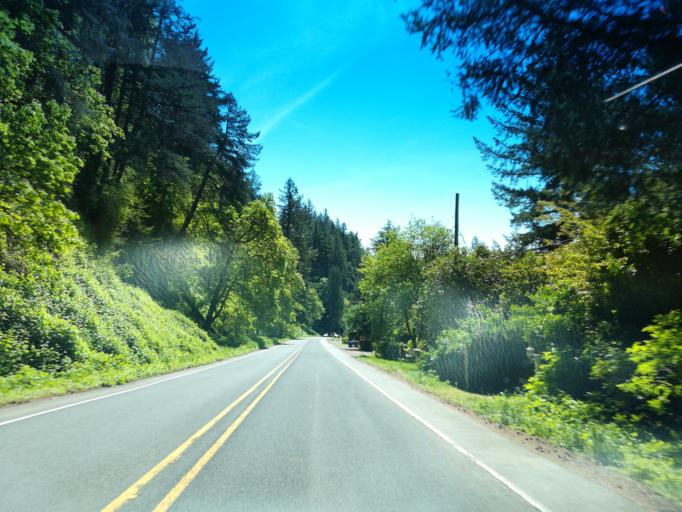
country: US
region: Oregon
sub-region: Multnomah County
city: Troutdale
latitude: 45.5186
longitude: -122.3681
